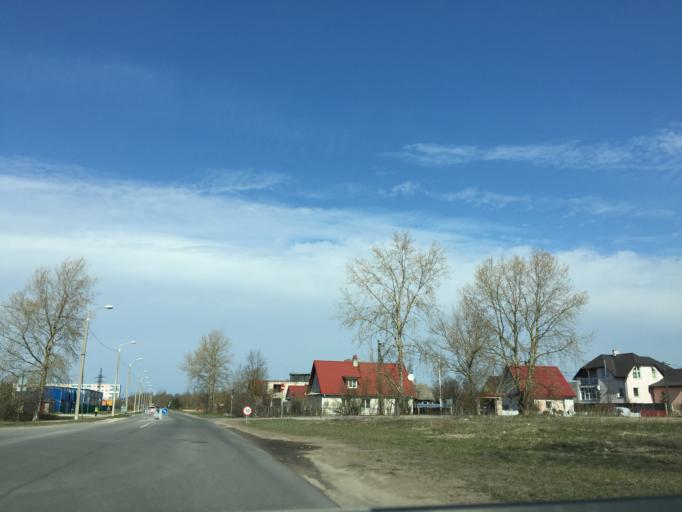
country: EE
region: Ida-Virumaa
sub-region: Narva linn
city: Narva
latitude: 59.3895
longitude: 28.1865
